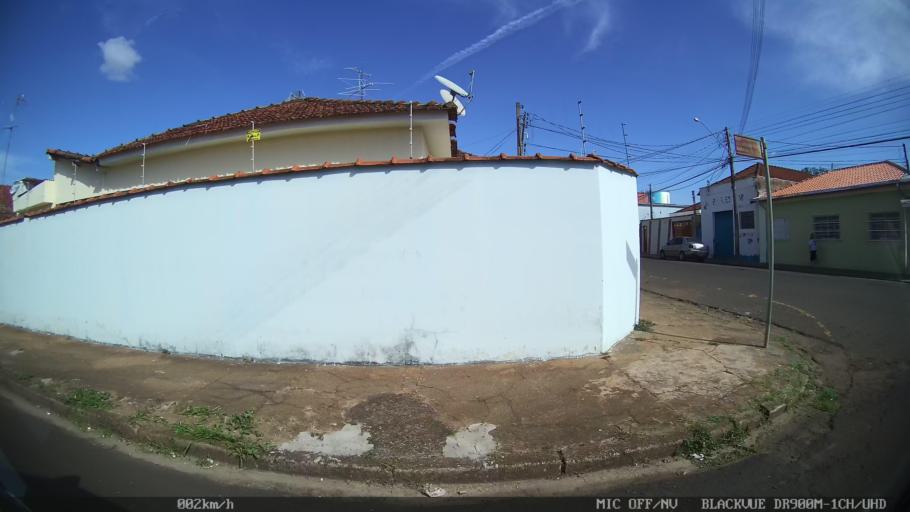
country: BR
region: Sao Paulo
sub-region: Franca
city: Franca
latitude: -20.5325
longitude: -47.4150
